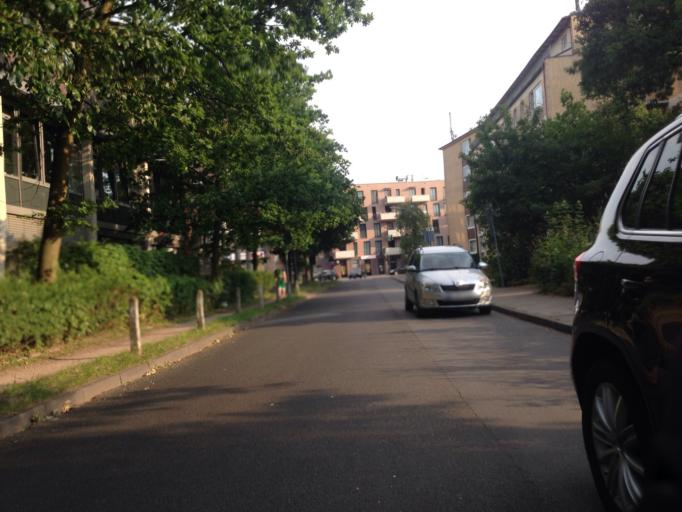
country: DE
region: Hamburg
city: Farmsen-Berne
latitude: 53.5862
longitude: 10.1280
